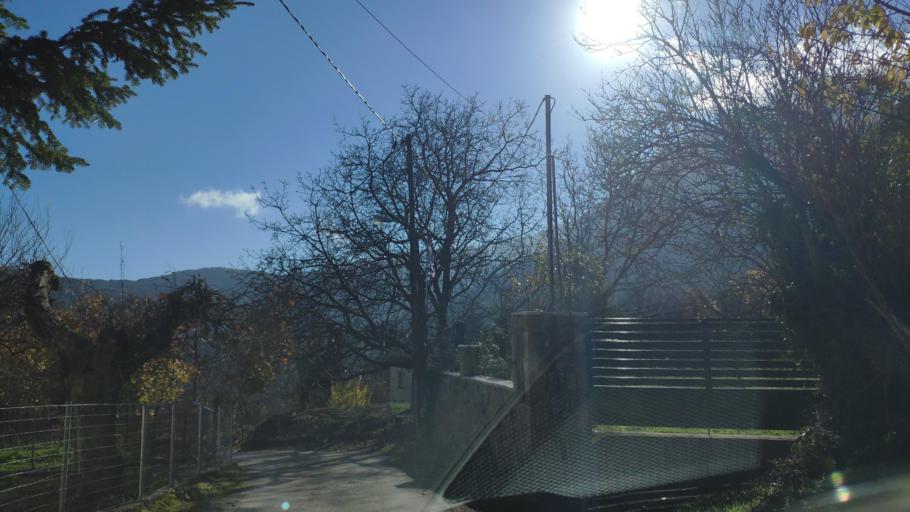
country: GR
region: West Greece
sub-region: Nomos Achaias
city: Aiyira
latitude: 38.0565
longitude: 22.4497
